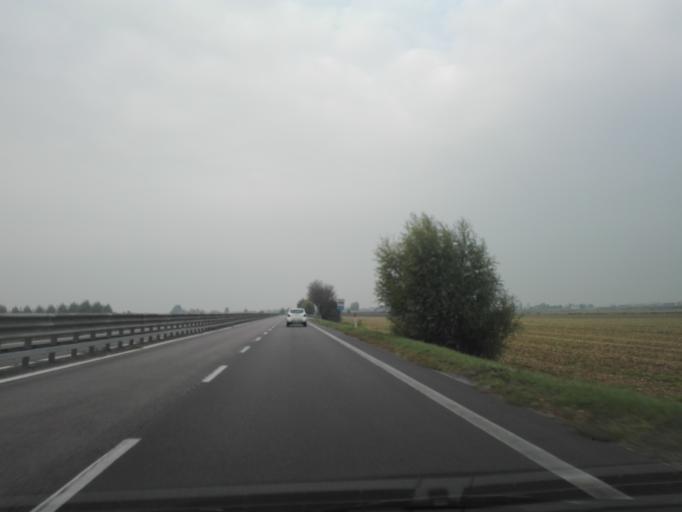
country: IT
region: Veneto
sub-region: Provincia di Verona
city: Villa Bartolomea
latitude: 45.1534
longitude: 11.3301
